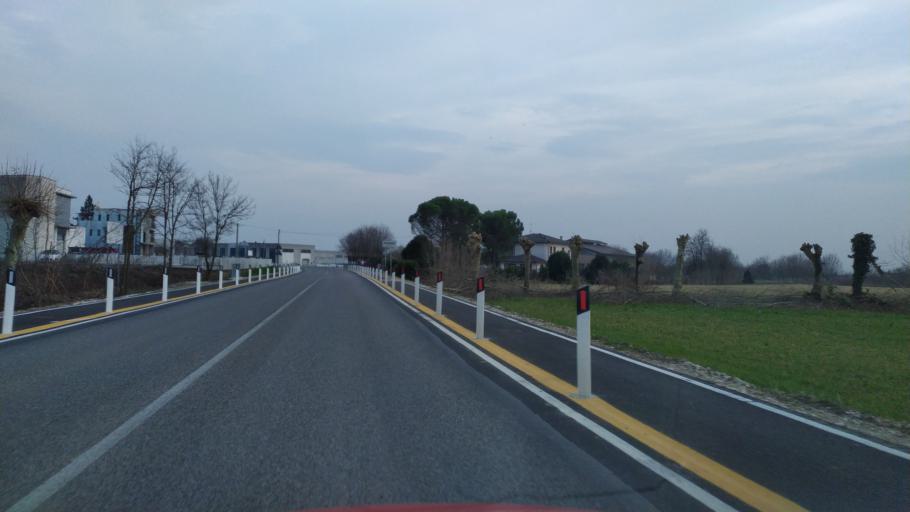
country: IT
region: Veneto
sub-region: Provincia di Vicenza
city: Dueville
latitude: 45.6268
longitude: 11.5644
